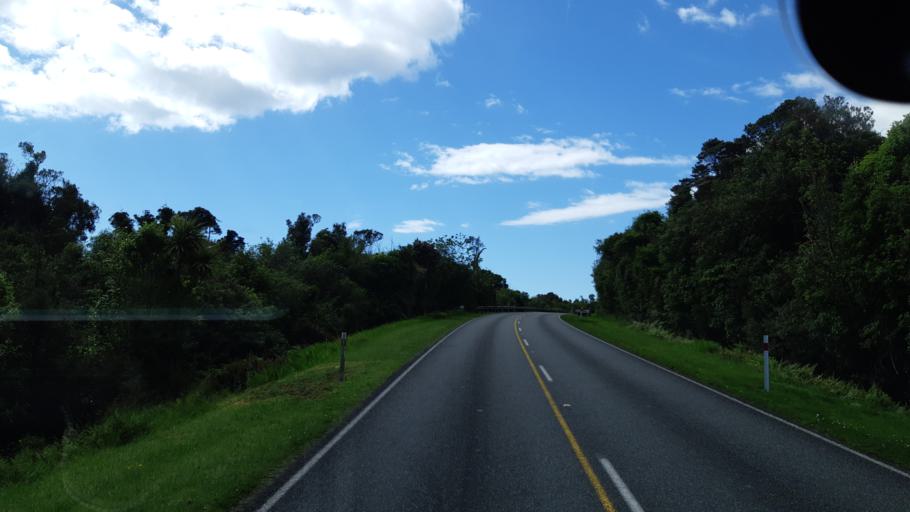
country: NZ
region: West Coast
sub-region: Westland District
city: Hokitika
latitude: -43.0705
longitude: 170.6273
